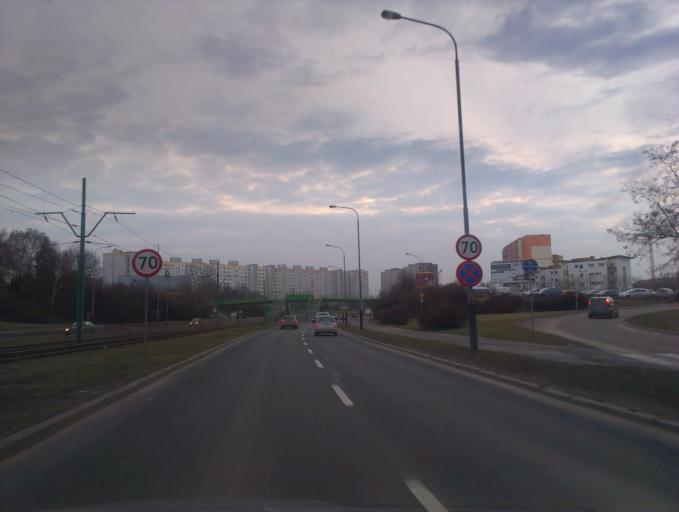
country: PL
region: Greater Poland Voivodeship
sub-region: Poznan
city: Poznan
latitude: 52.3817
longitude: 16.9671
